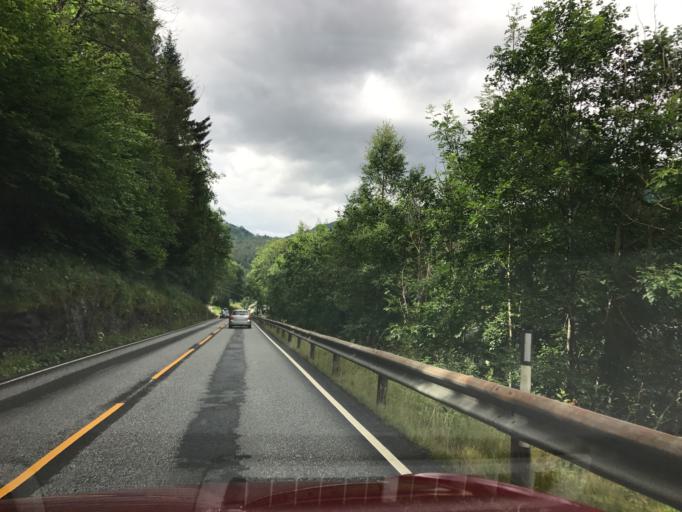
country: NO
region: Hordaland
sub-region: Granvin
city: Granvin
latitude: 60.5462
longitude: 6.7253
